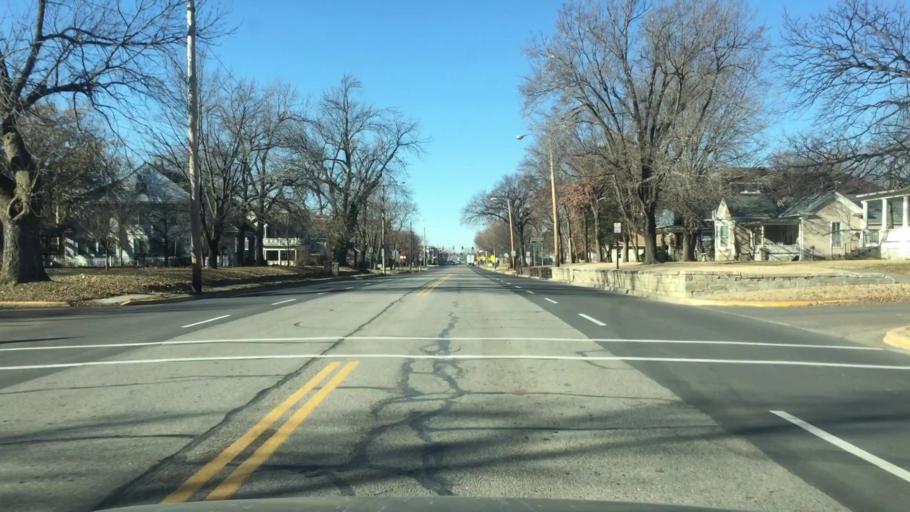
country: US
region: Kansas
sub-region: Allen County
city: Iola
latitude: 37.9214
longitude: -95.3974
